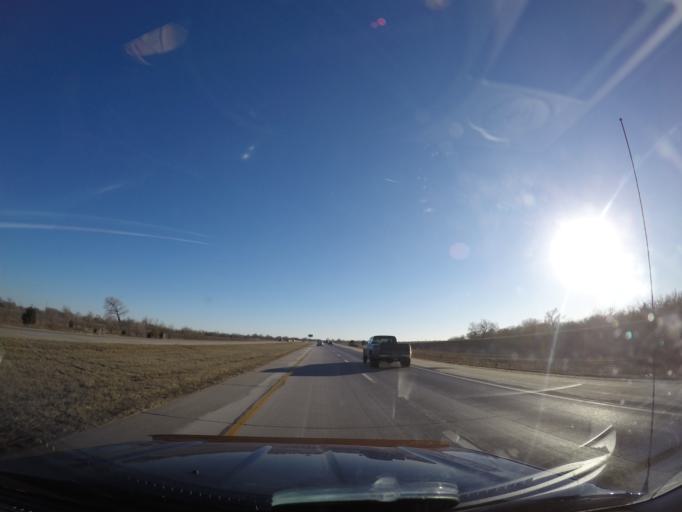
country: US
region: Kansas
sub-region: Sedgwick County
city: Wichita
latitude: 37.7441
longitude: -97.3749
